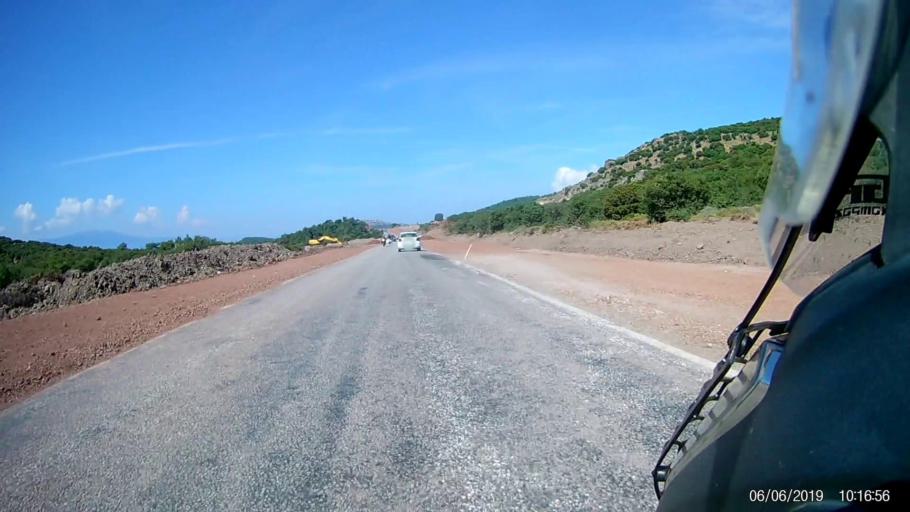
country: TR
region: Canakkale
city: Ayvacik
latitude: 39.5255
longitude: 26.4753
